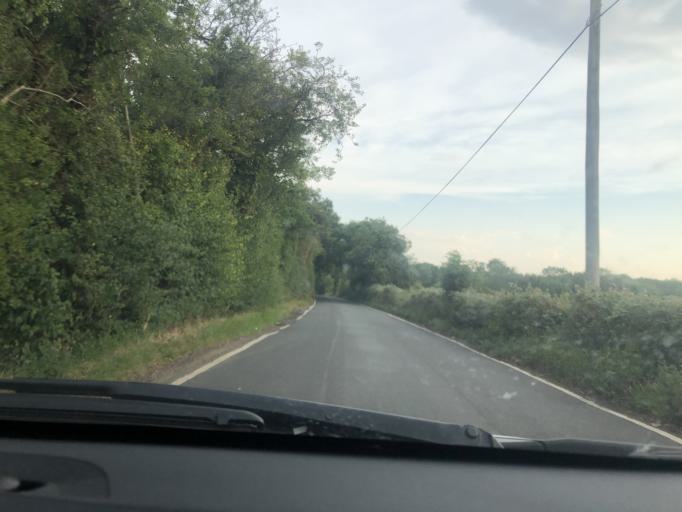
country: GB
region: England
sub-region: Kent
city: Sturry
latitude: 51.3116
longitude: 1.1372
